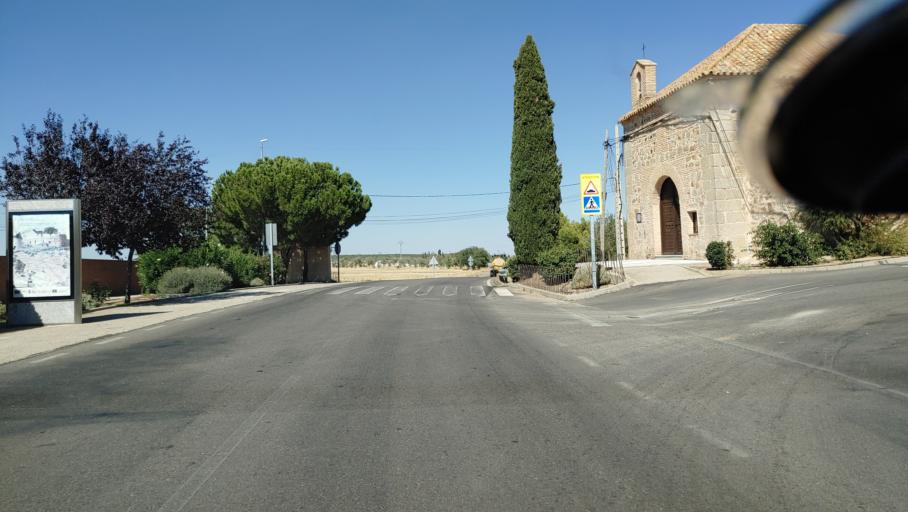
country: ES
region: Castille-La Mancha
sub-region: Province of Toledo
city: Pulgar
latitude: 39.6972
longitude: -4.1500
